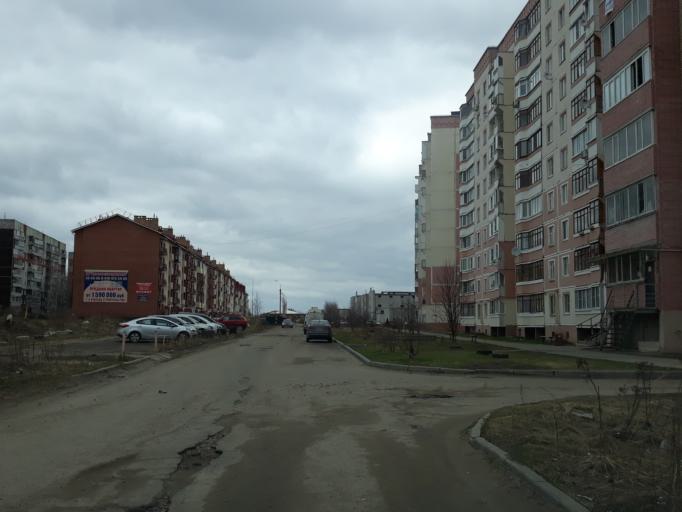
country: RU
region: Jaroslavl
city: Yaroslavl
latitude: 57.6494
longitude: 39.9688
